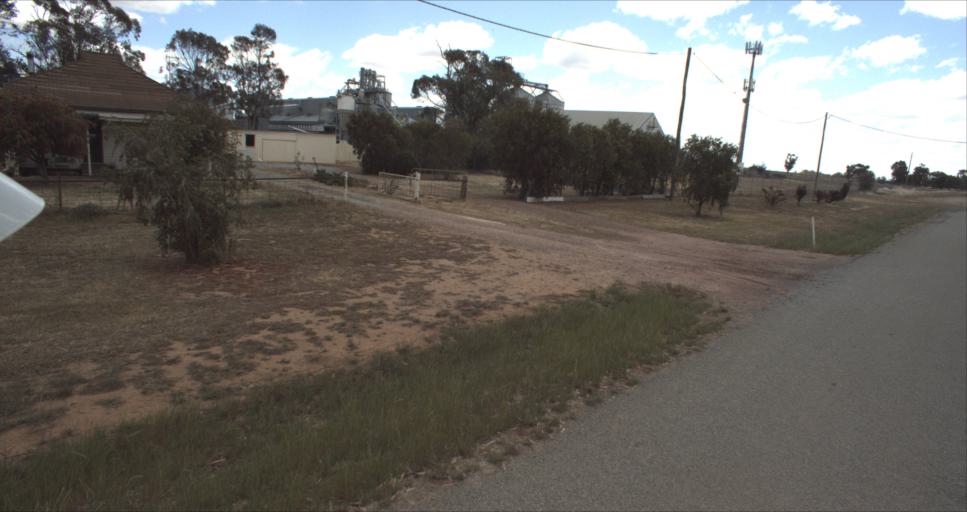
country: AU
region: New South Wales
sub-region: Murrumbidgee Shire
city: Darlington Point
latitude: -34.5147
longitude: 146.1826
